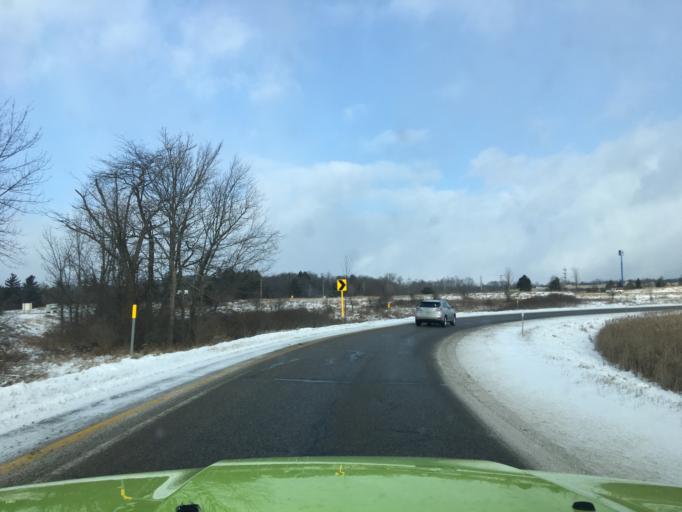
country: US
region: Michigan
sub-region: Mecosta County
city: Big Rapids
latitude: 43.6877
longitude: -85.5240
